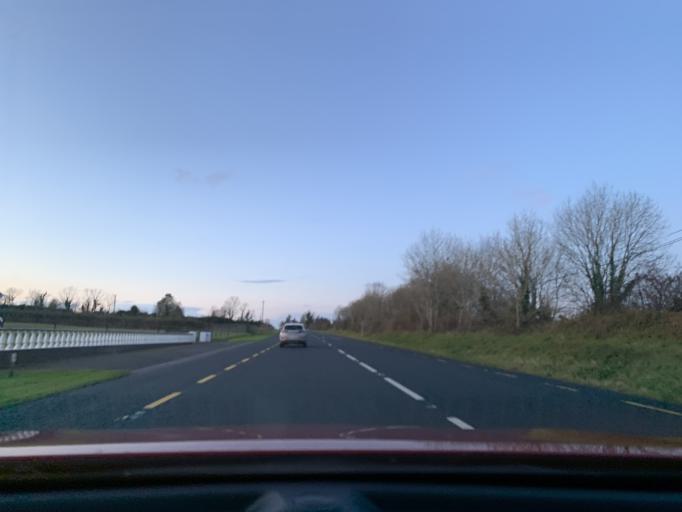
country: IE
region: Connaught
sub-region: County Leitrim
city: Carrick-on-Shannon
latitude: 53.8899
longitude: -7.9454
